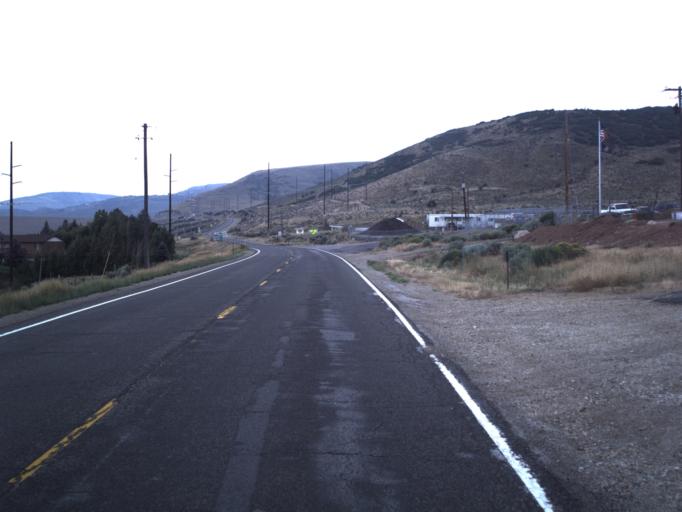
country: US
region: Utah
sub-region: Summit County
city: Coalville
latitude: 40.8028
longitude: -111.4087
